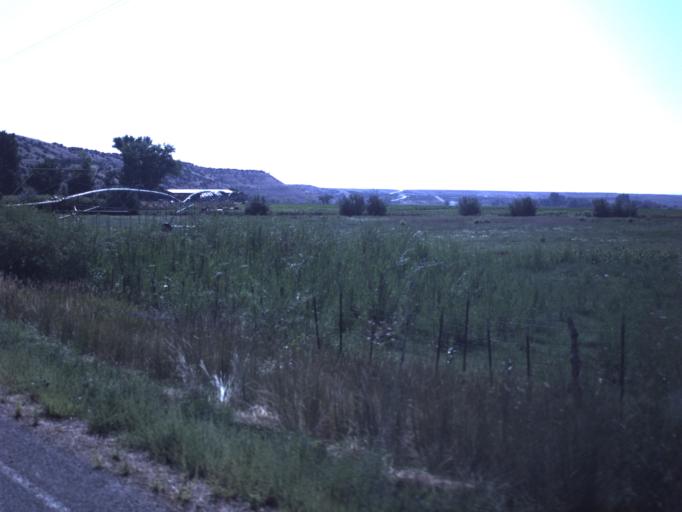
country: US
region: Utah
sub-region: Duchesne County
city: Duchesne
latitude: 40.2708
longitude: -110.4265
